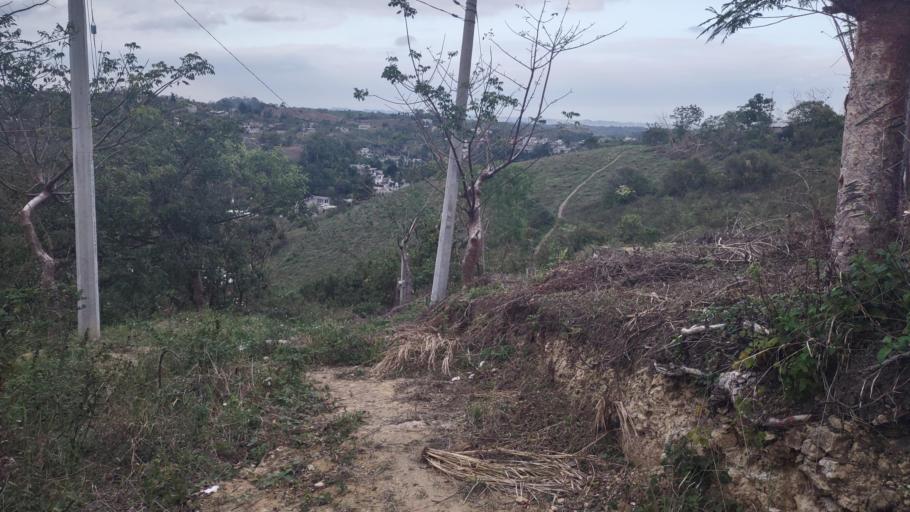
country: MX
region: Veracruz
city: Papantla de Olarte
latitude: 20.4536
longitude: -97.3106
